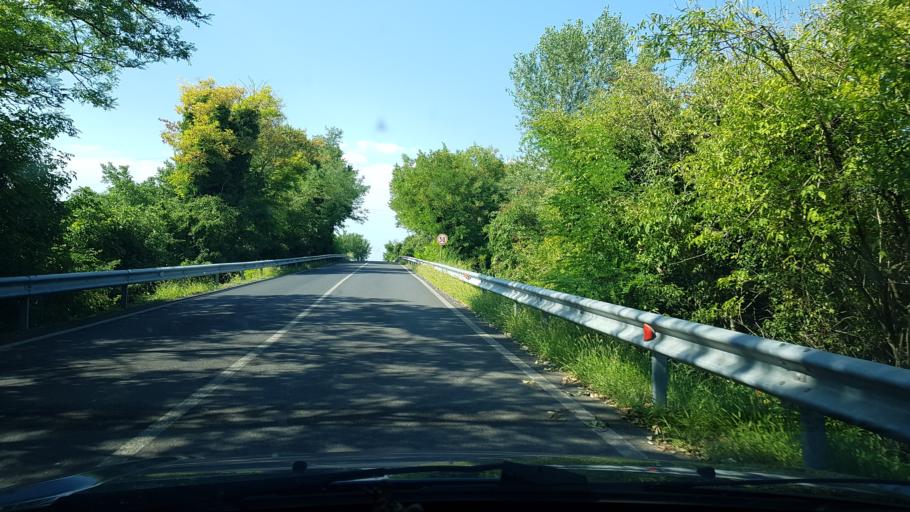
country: IT
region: Friuli Venezia Giulia
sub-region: Provincia di Gorizia
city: Staranzano
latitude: 45.7885
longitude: 13.5066
